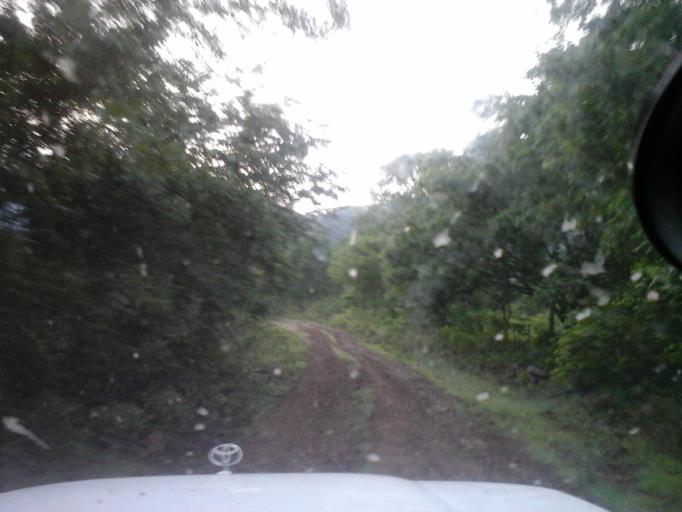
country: CO
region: Cesar
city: Agustin Codazzi
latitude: 10.1716
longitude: -73.1639
